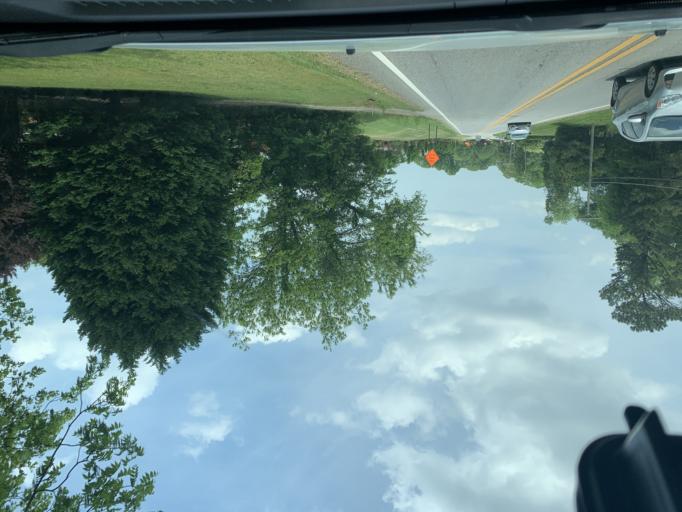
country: US
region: Georgia
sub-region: Forsyth County
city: Cumming
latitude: 34.1446
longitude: -84.1482
